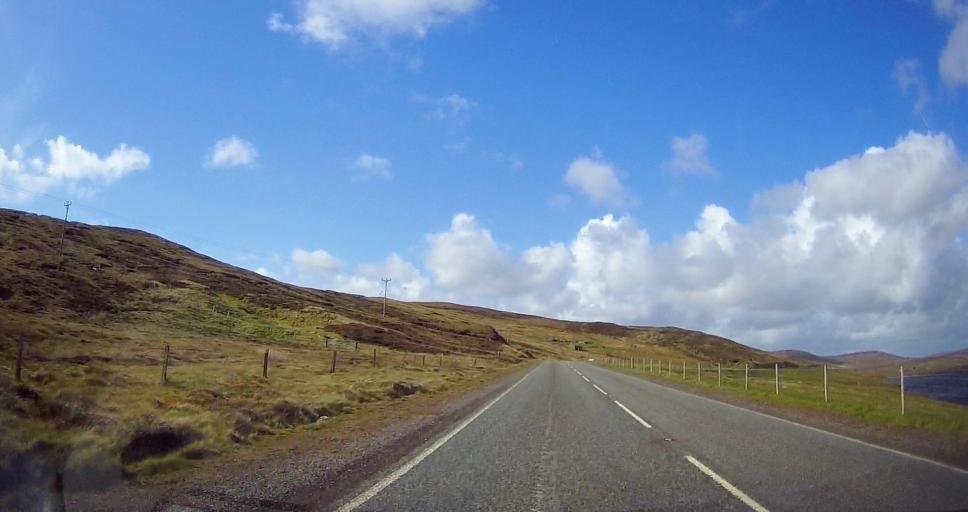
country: GB
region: Scotland
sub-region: Shetland Islands
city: Lerwick
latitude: 60.2526
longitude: -1.2260
